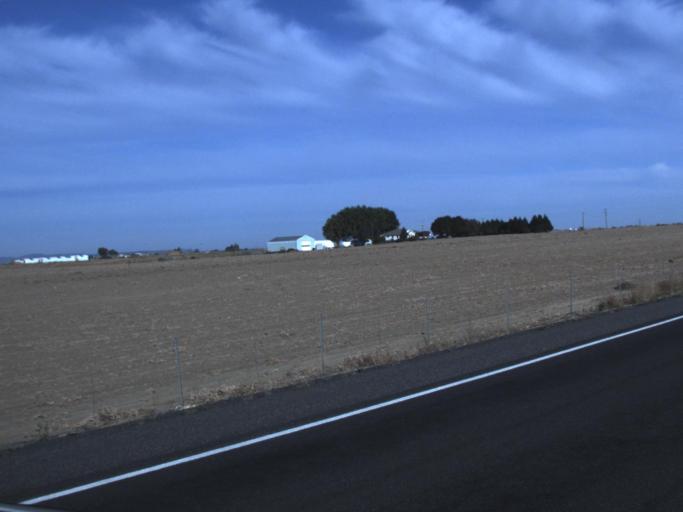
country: US
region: Washington
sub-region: Franklin County
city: Basin City
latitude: 46.6163
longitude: -119.0062
